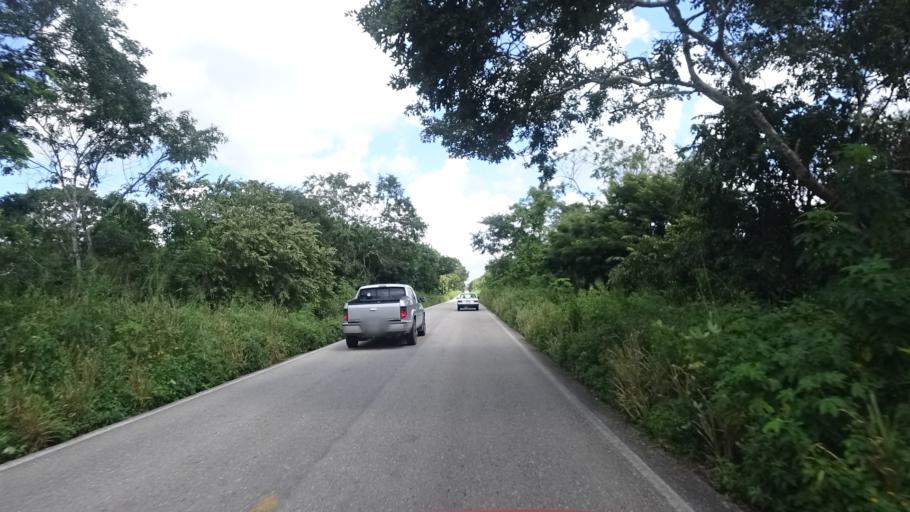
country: MX
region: Yucatan
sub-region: Panaba
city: Loche
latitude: 21.3932
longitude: -88.1422
